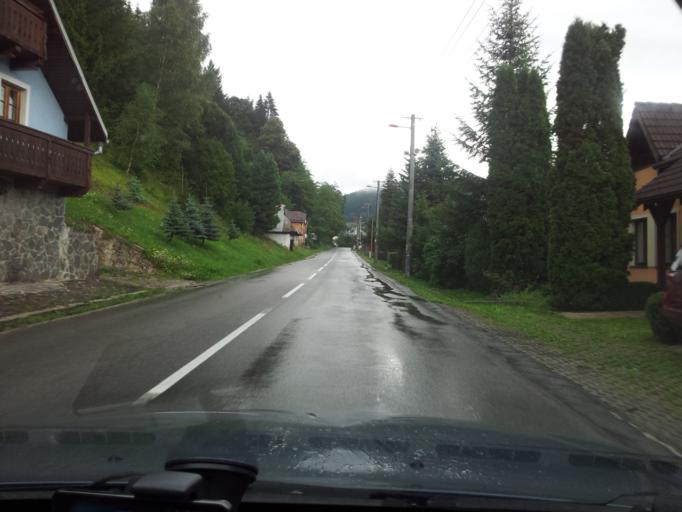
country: SK
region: Banskobystricky
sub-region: Okres Banska Bystrica
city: Brezno
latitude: 48.8485
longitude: 19.6284
